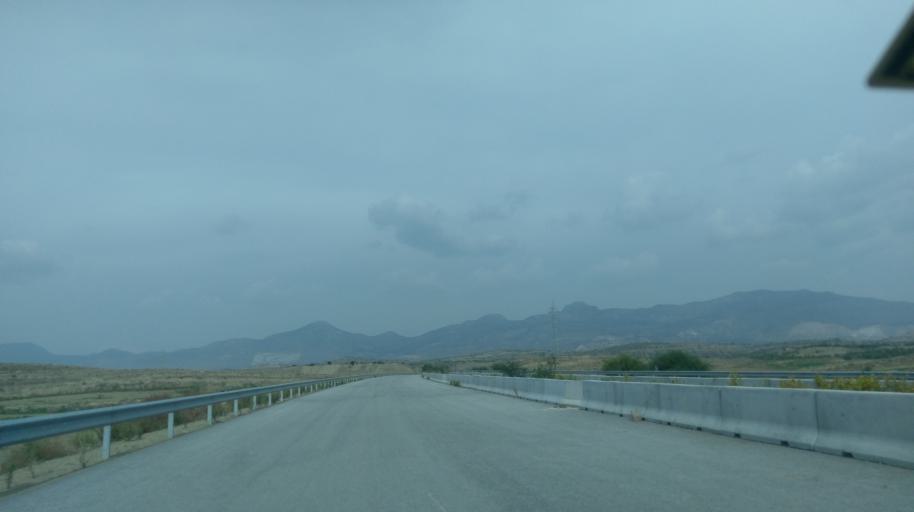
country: CY
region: Lefkosia
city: Nicosia
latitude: 35.2238
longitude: 33.4003
